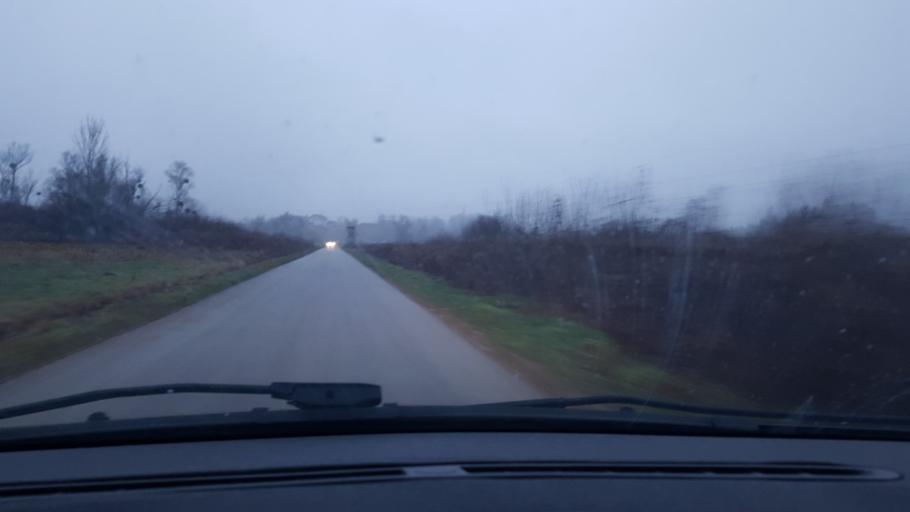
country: HR
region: Krapinsko-Zagorska
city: Zabok
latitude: 46.0410
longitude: 15.9228
